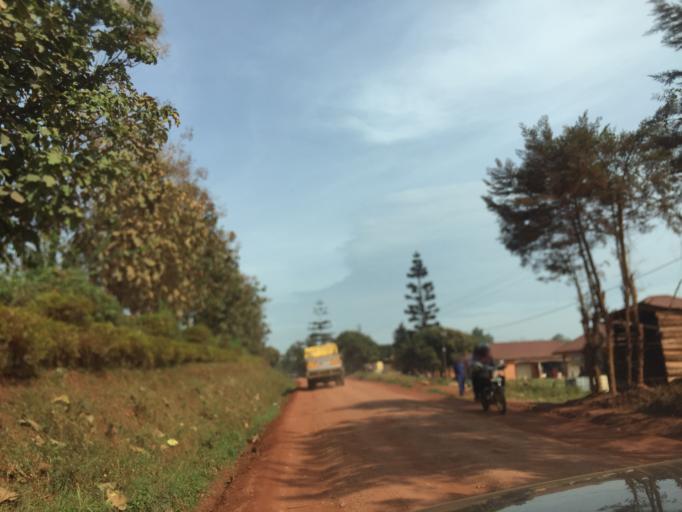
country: UG
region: Central Region
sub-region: Wakiso District
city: Wakiso
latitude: 0.4609
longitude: 32.5585
